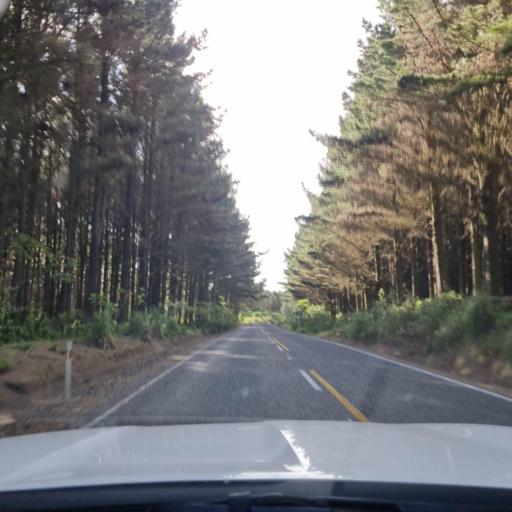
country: NZ
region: Northland
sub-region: Kaipara District
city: Dargaville
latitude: -36.2429
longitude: 174.0463
